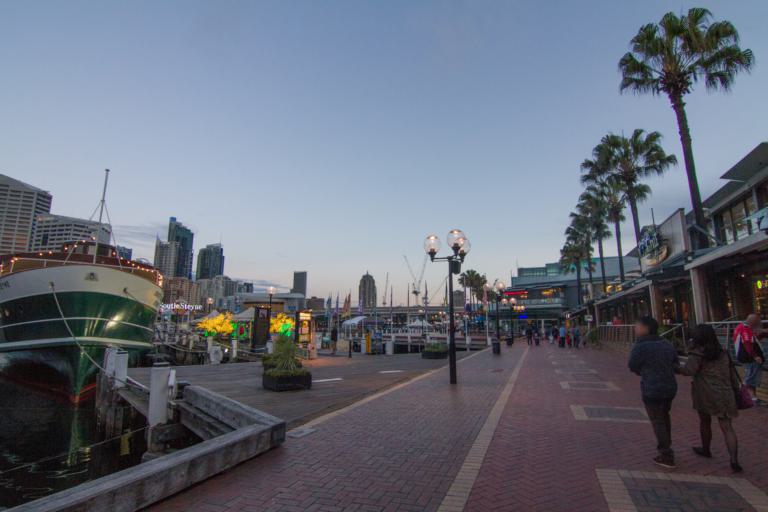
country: AU
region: New South Wales
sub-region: City of Sydney
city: Sydney
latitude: -33.8708
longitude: 151.1992
